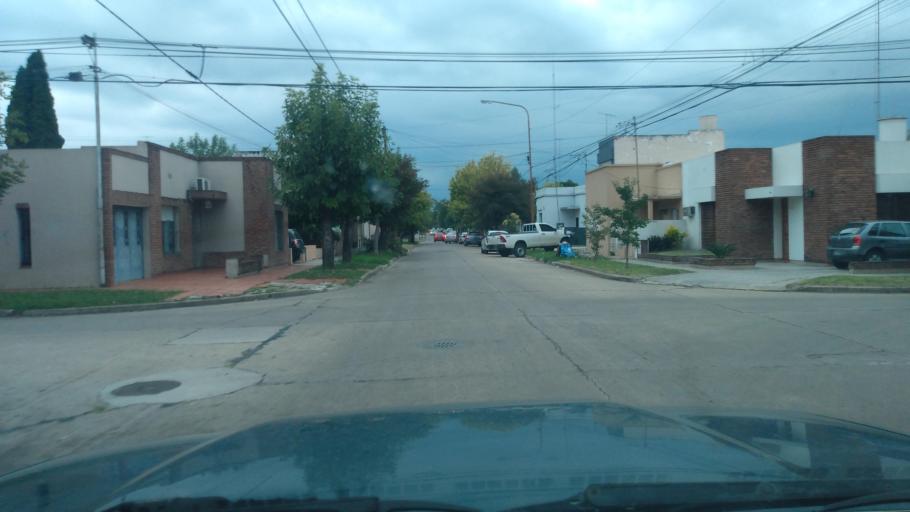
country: AR
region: Buenos Aires
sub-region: Partido de Lujan
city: Lujan
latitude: -34.5689
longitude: -59.1005
